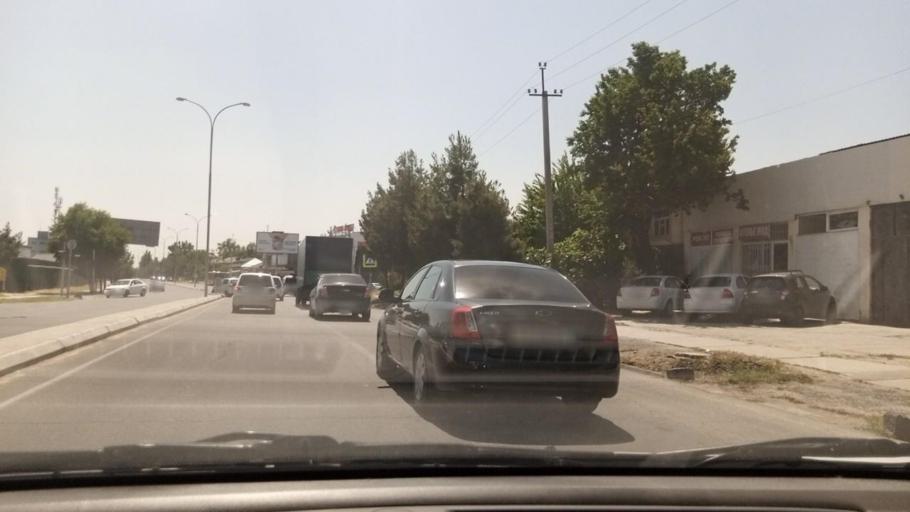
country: UZ
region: Toshkent Shahri
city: Tashkent
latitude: 41.2270
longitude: 69.1804
